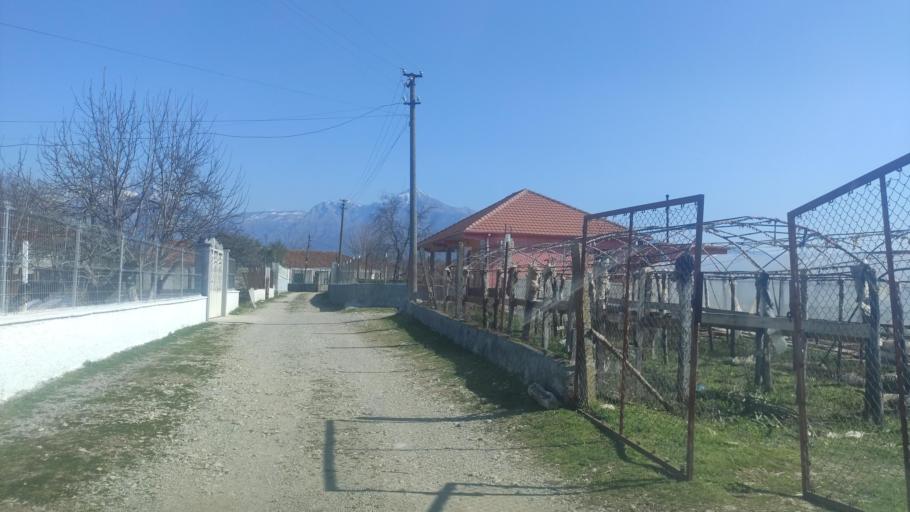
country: AL
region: Shkoder
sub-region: Rrethi i Malesia e Madhe
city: Grude-Fushe
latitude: 42.1707
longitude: 19.4807
